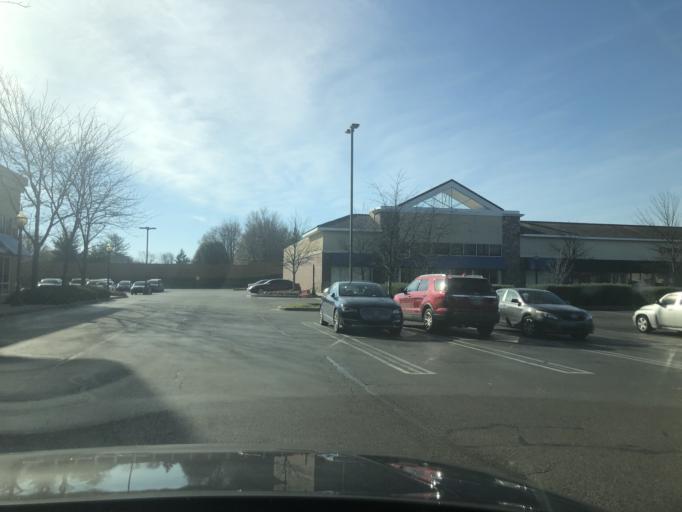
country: US
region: Indiana
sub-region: Vanderburgh County
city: Melody Hill
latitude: 37.9741
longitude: -87.4705
